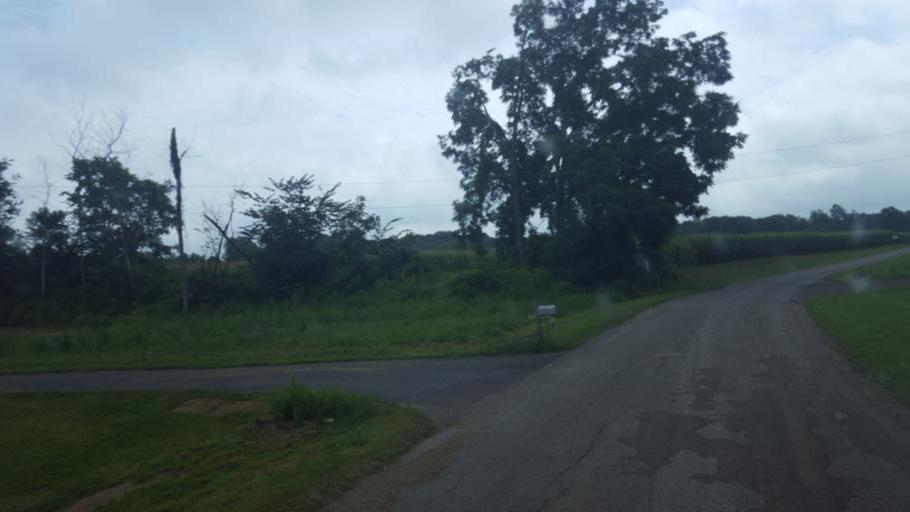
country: US
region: Ohio
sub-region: Morrow County
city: Mount Gilead
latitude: 40.5326
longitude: -82.7020
